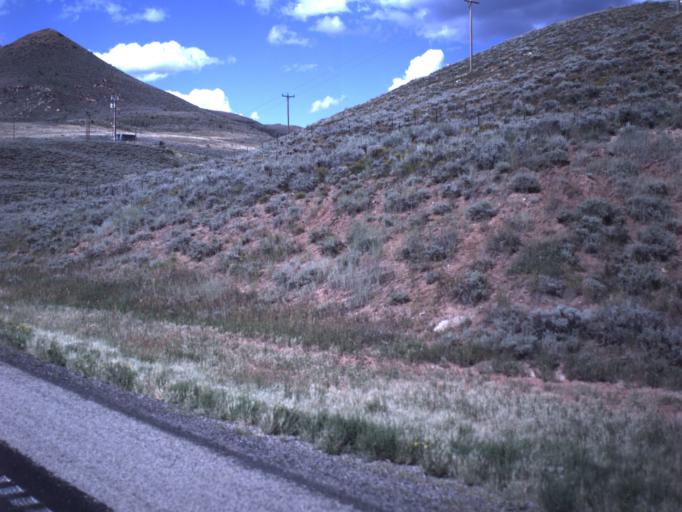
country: US
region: Utah
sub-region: Wasatch County
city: Heber
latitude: 40.2177
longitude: -111.1038
